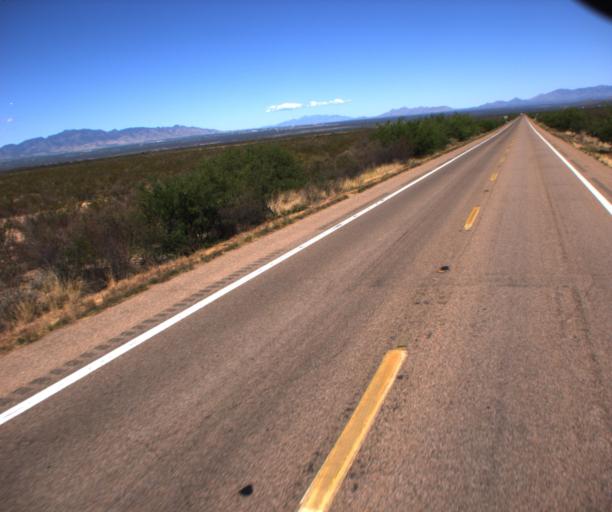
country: US
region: Arizona
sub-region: Cochise County
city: Bisbee
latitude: 31.5278
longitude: -110.0511
